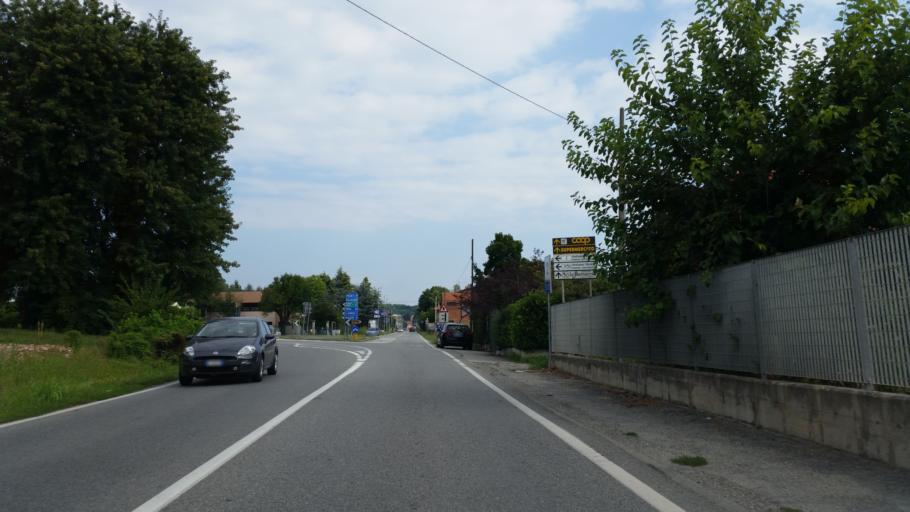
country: IT
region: Piedmont
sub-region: Provincia di Torino
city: Caluso
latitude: 45.2954
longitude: 7.8909
